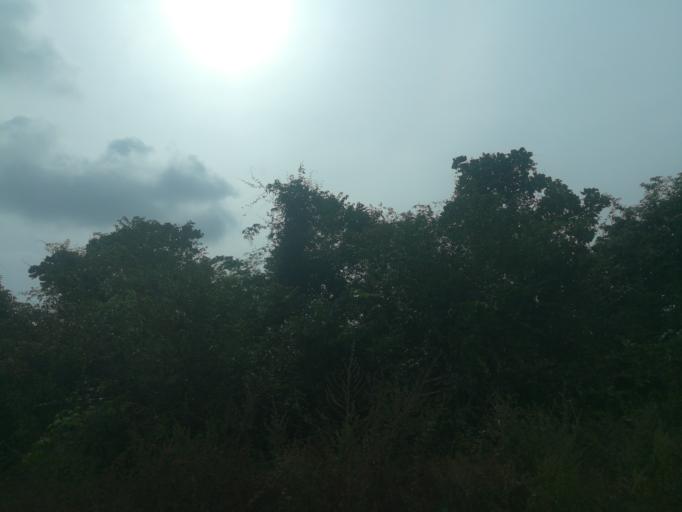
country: NG
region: Ogun
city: Ayetoro
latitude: 7.2937
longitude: 3.0787
